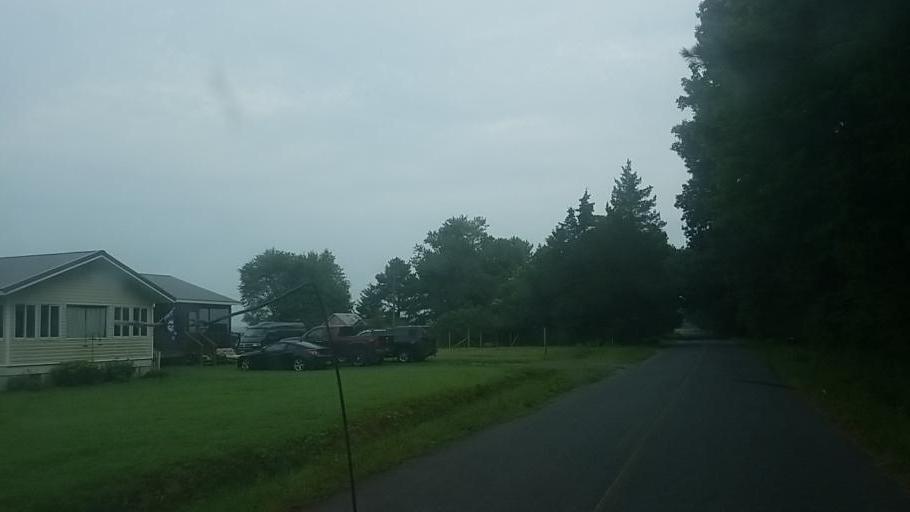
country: US
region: Delaware
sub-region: Sussex County
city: Selbyville
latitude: 38.4278
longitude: -75.2880
